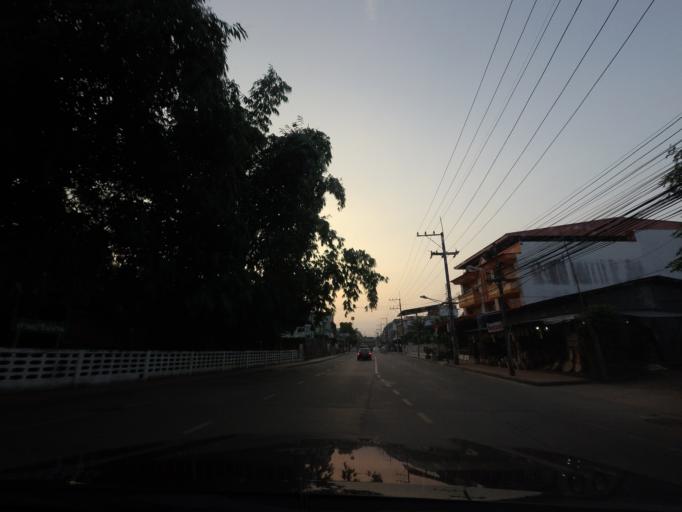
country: TH
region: Nan
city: Nan
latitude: 18.7763
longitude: 100.7777
